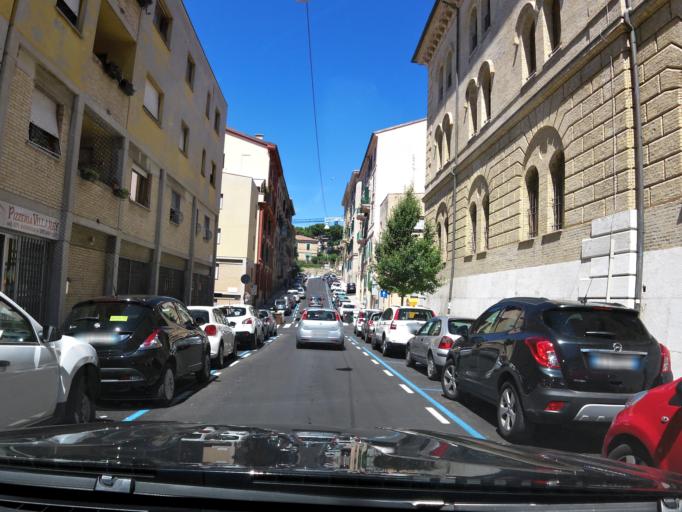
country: IT
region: The Marches
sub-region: Provincia di Ancona
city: Le Grazie di Ancona
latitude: 43.6200
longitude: 13.5171
